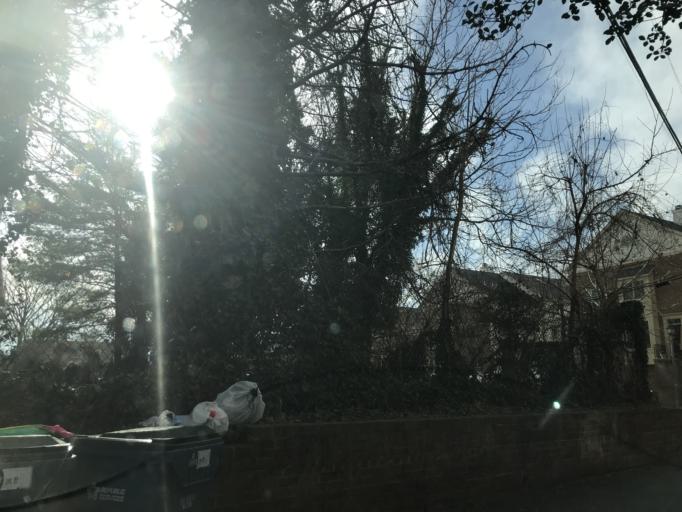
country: US
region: Virginia
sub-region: Arlington County
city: Arlington
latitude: 38.8961
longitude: -77.0930
